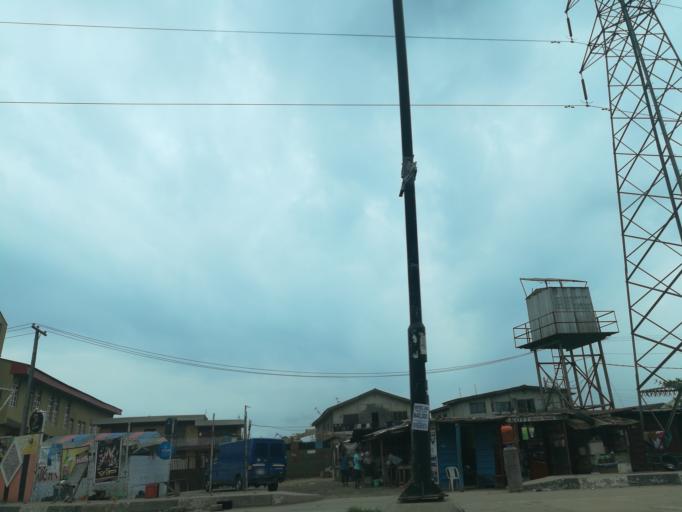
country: NG
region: Lagos
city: Ojota
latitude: 6.6178
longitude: 3.3972
